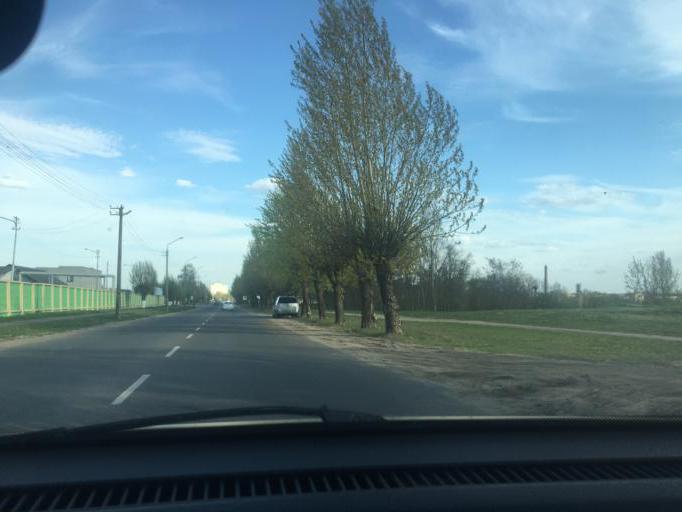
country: BY
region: Mogilev
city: Babruysk
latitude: 53.1565
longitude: 29.1758
